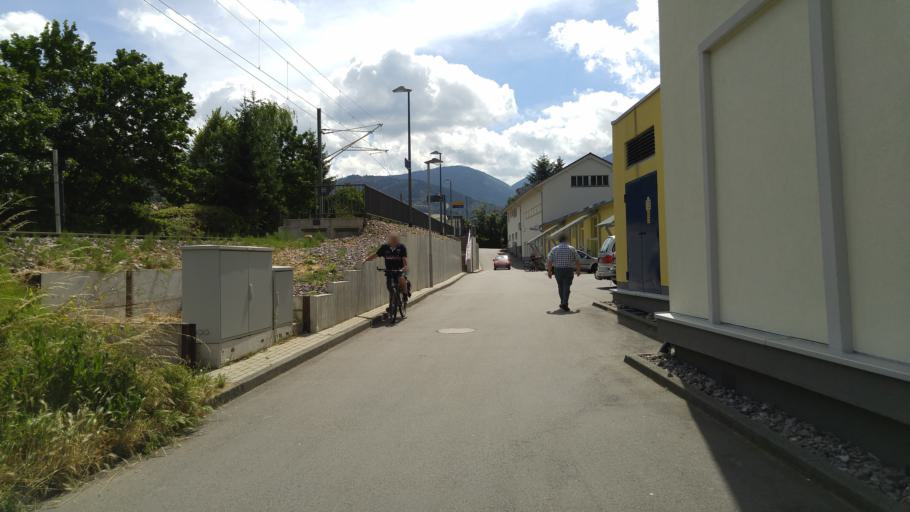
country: DE
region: Baden-Wuerttemberg
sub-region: Freiburg Region
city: Muenstertal/Schwarzwald
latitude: 47.8597
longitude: 7.7621
